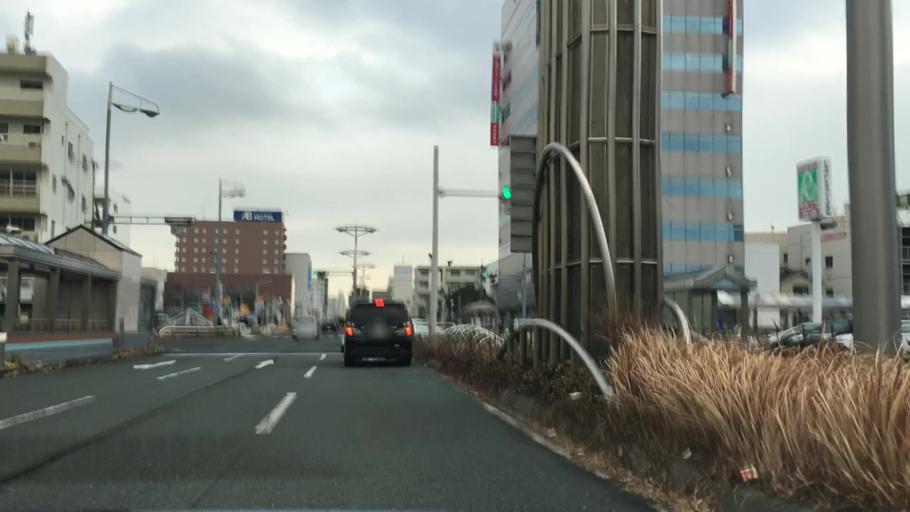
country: JP
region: Aichi
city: Toyohashi
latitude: 34.7624
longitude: 137.3794
